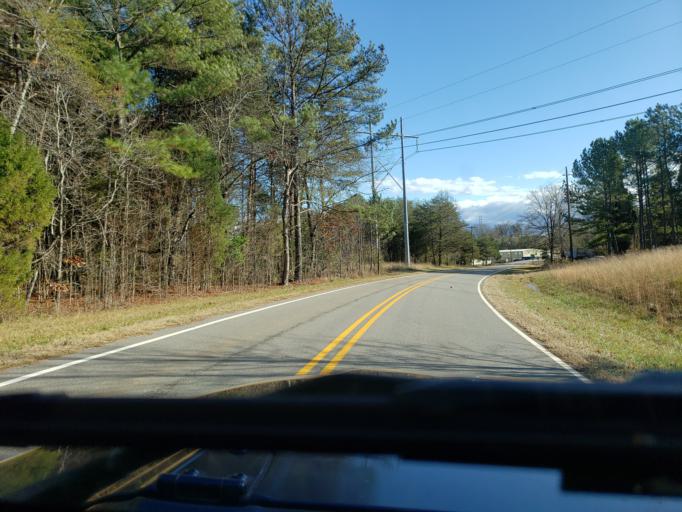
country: US
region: North Carolina
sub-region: Cleveland County
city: White Plains
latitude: 35.1681
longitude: -81.4282
